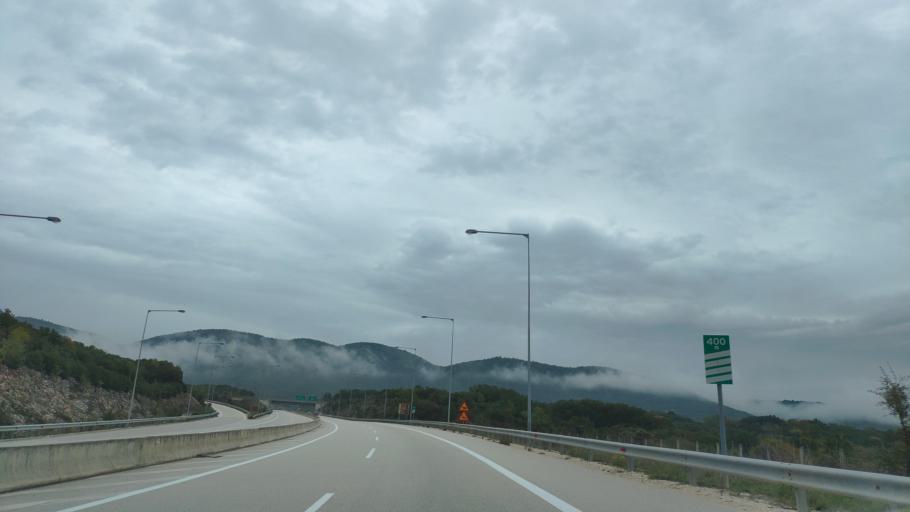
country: GR
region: Epirus
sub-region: Nomos Ioanninon
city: Pedini
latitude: 39.5568
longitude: 20.7716
